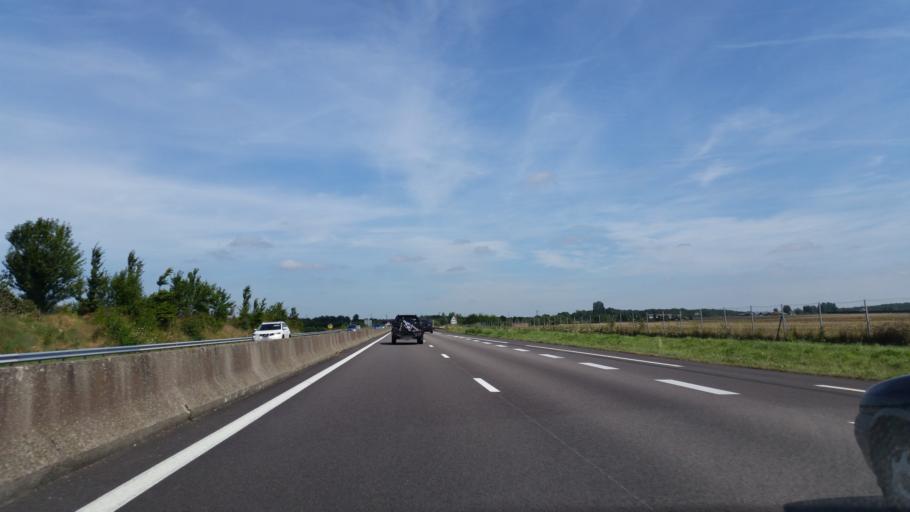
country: FR
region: Haute-Normandie
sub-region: Departement de la Seine-Maritime
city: Aumale
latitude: 49.7651
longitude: 1.7086
